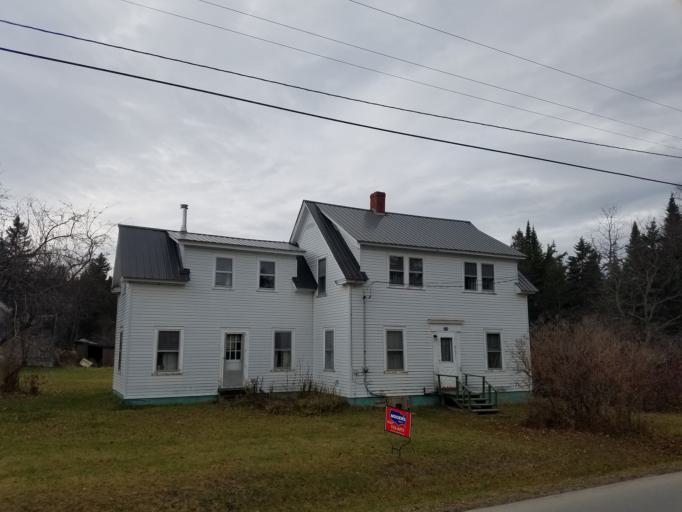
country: US
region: Maine
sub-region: Aroostook County
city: Hodgdon
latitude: 46.1268
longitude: -68.1646
